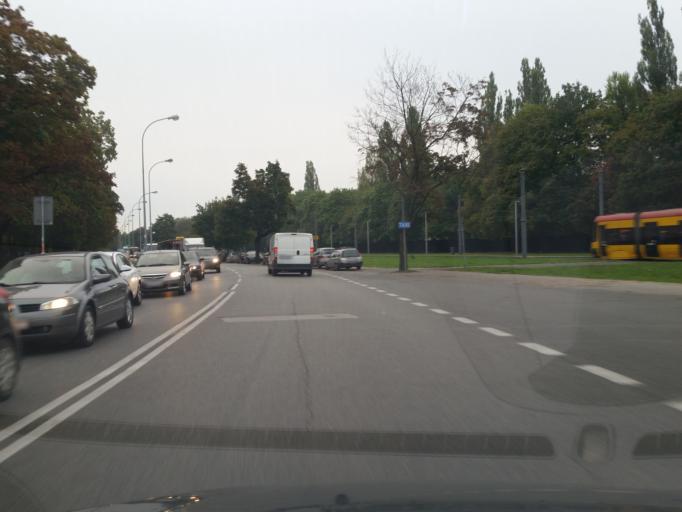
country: PL
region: Masovian Voivodeship
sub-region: Warszawa
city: Praga Polnoc
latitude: 52.2625
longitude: 21.0220
